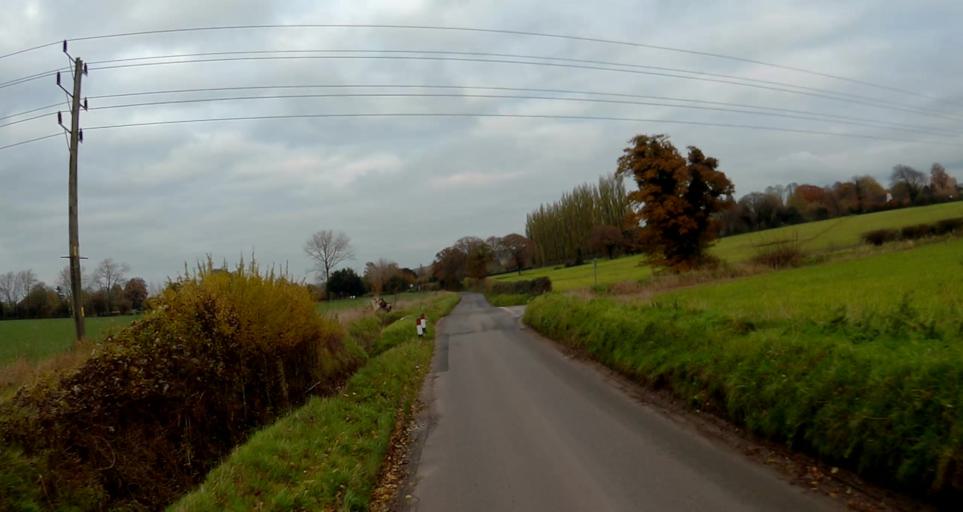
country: GB
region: England
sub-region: Hampshire
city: Fleet
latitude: 51.2301
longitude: -0.8698
